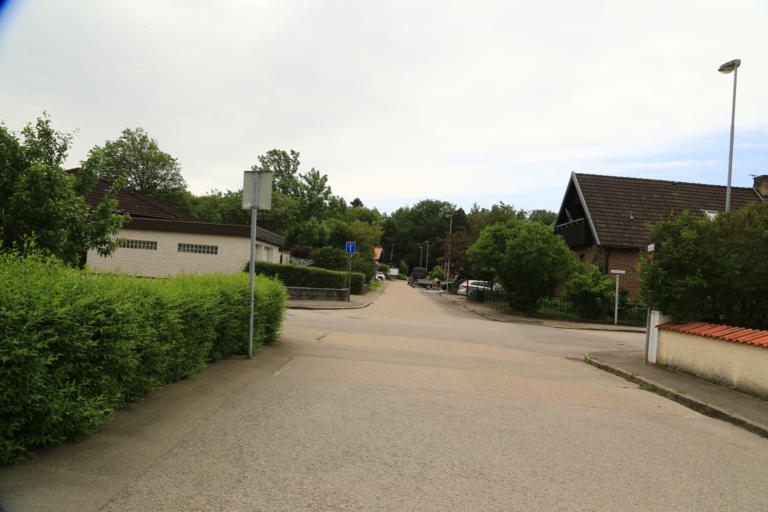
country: SE
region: Halland
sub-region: Varbergs Kommun
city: Varberg
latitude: 57.1009
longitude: 12.2700
